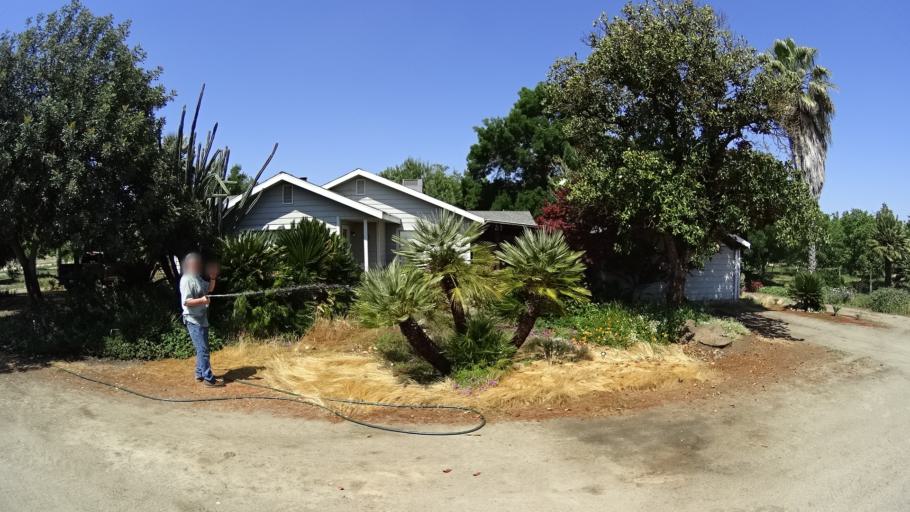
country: US
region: California
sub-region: Fresno County
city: Kingsburg
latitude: 36.4650
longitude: -119.5734
